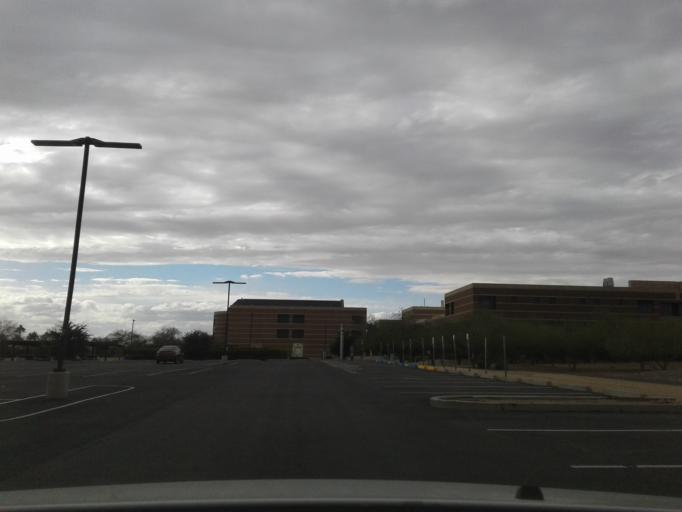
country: US
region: Arizona
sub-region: Maricopa County
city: Glendale
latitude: 33.6072
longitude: -112.1573
